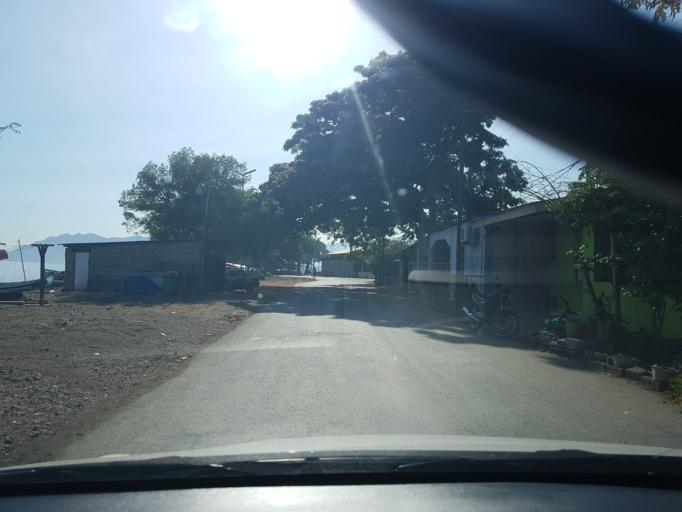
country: TL
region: Dili
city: Dili
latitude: -8.5410
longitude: 125.5421
